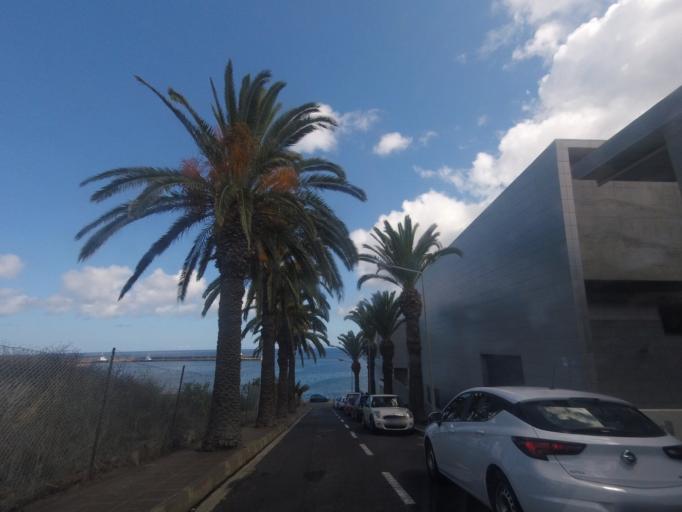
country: PT
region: Madeira
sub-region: Machico
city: Canical
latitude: 32.7363
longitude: -16.7406
